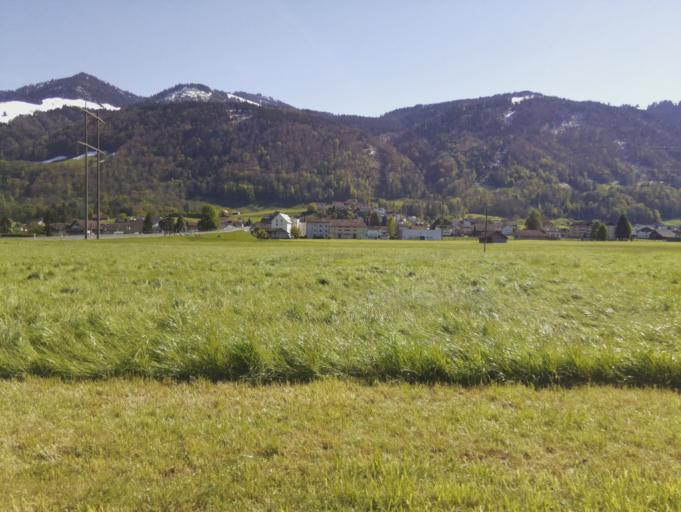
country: CH
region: Schwyz
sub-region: Bezirk March
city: Schubelbach
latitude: 47.1799
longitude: 8.9411
